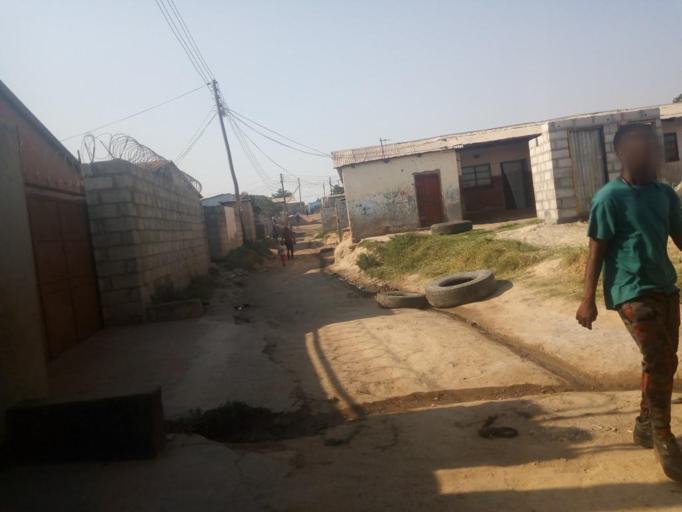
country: ZM
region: Lusaka
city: Lusaka
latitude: -15.4027
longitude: 28.3725
